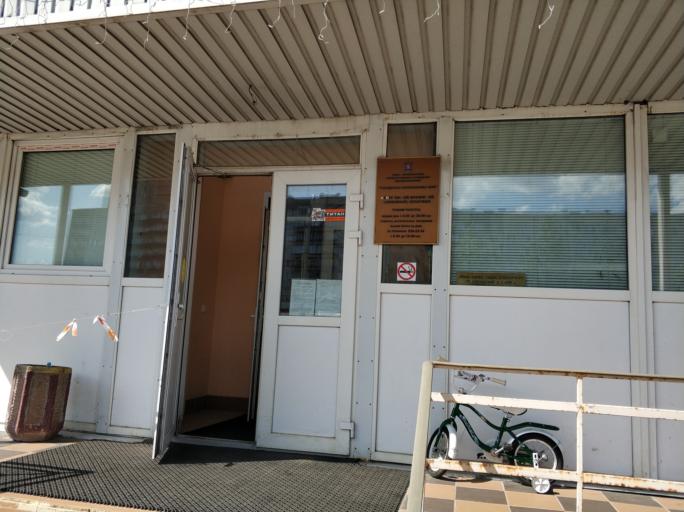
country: RU
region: St.-Petersburg
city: Grazhdanka
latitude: 60.0273
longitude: 30.4113
